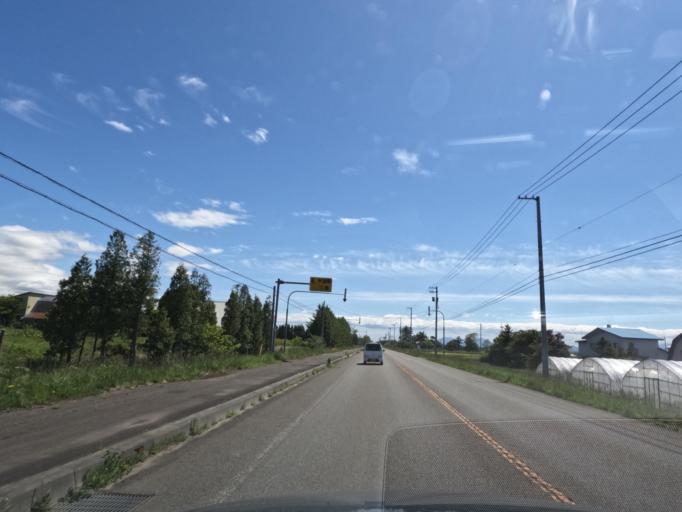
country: JP
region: Hokkaido
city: Kitahiroshima
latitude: 43.0381
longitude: 141.7195
